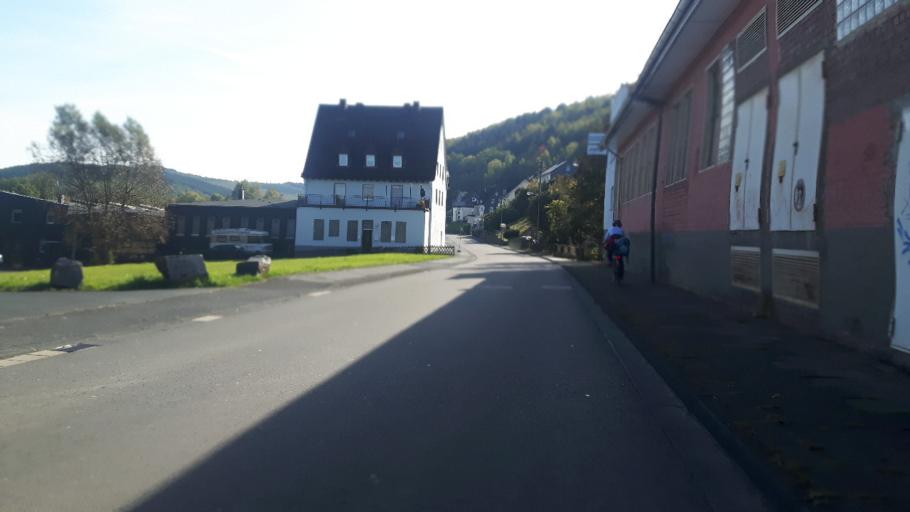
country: DE
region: North Rhine-Westphalia
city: Netphen
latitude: 50.8826
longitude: 8.1350
